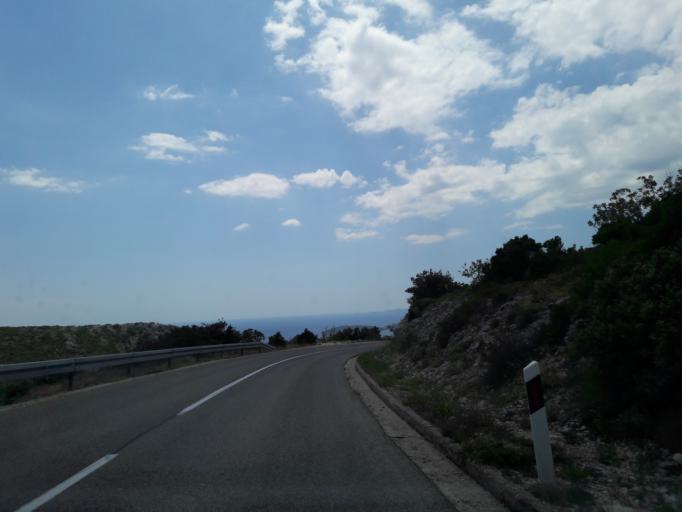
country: HR
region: Dubrovacko-Neretvanska
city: Orebic
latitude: 42.9728
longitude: 17.2660
